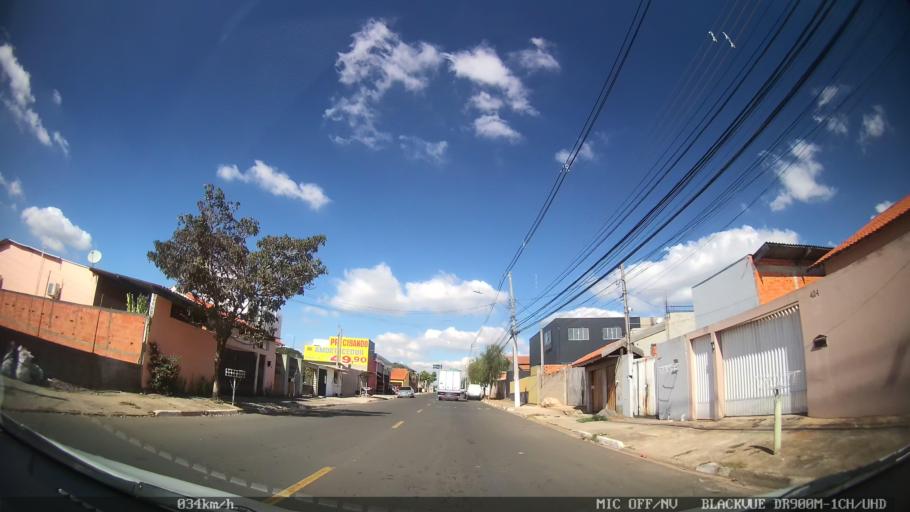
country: BR
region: Sao Paulo
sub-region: Hortolandia
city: Hortolandia
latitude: -22.8880
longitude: -47.2224
